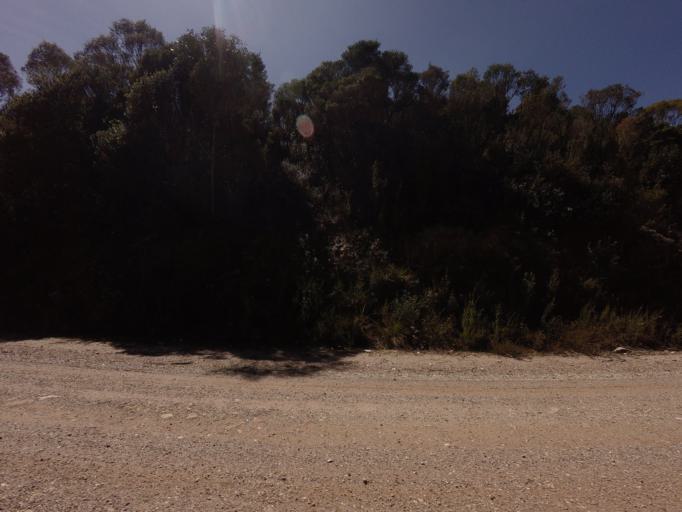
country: AU
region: Tasmania
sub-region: Huon Valley
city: Geeveston
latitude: -43.0066
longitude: 146.3577
